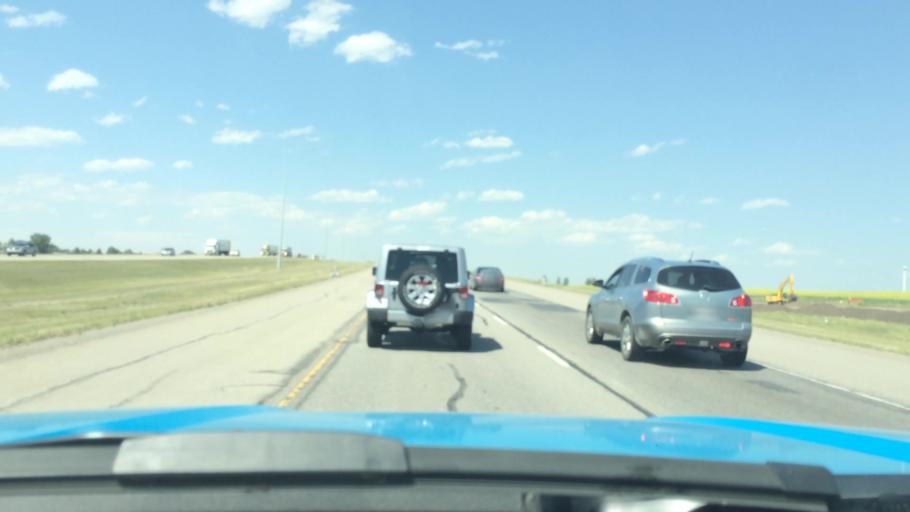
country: CA
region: Alberta
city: Chestermere
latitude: 51.0519
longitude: -113.9203
